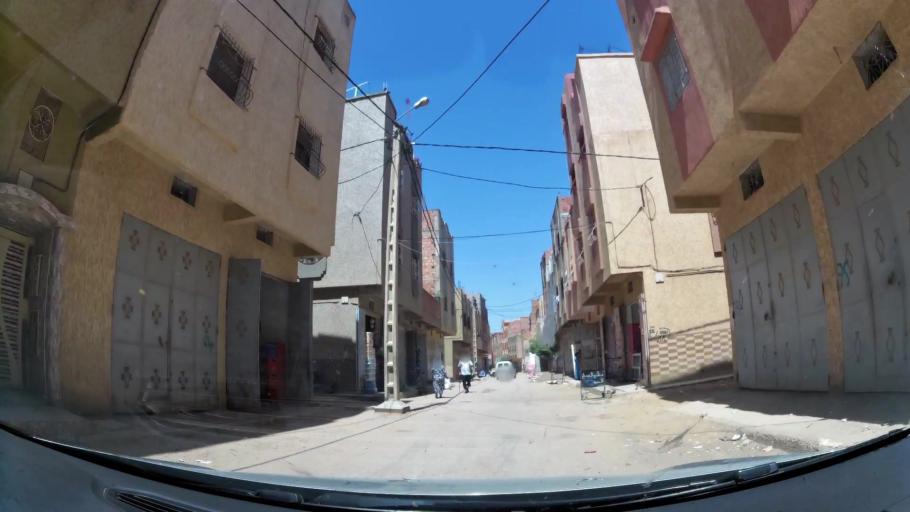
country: MA
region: Rabat-Sale-Zemmour-Zaer
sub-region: Khemisset
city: Khemisset
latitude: 33.8126
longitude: -6.0698
